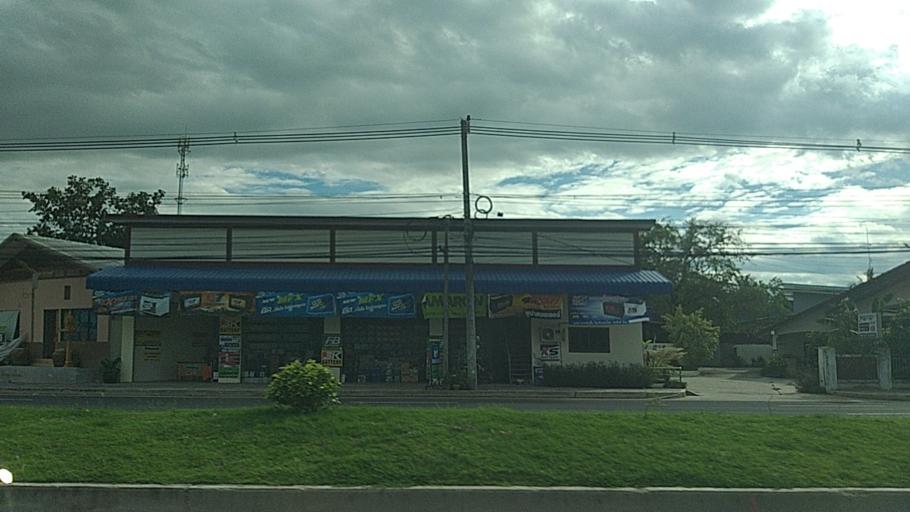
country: TH
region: Surin
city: Prasat
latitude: 14.6173
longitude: 103.4152
